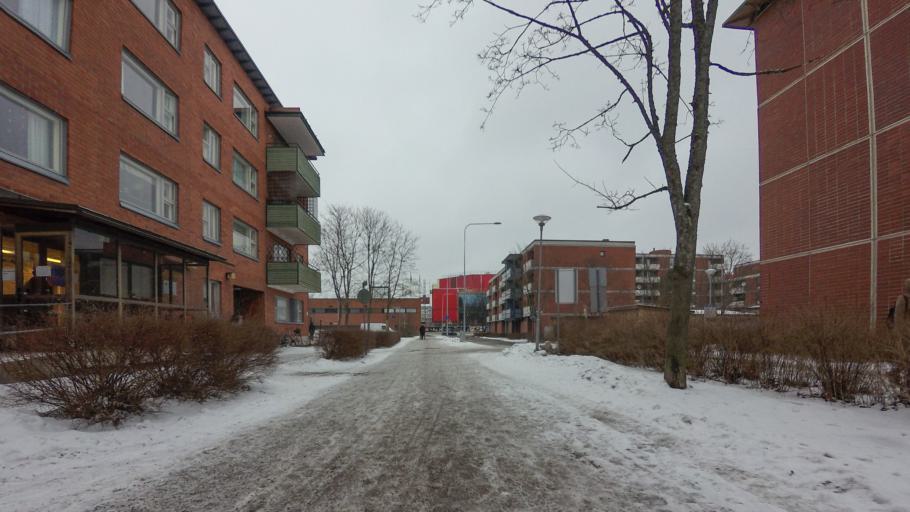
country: FI
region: Uusimaa
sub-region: Helsinki
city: Vantaa
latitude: 60.2080
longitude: 25.0869
